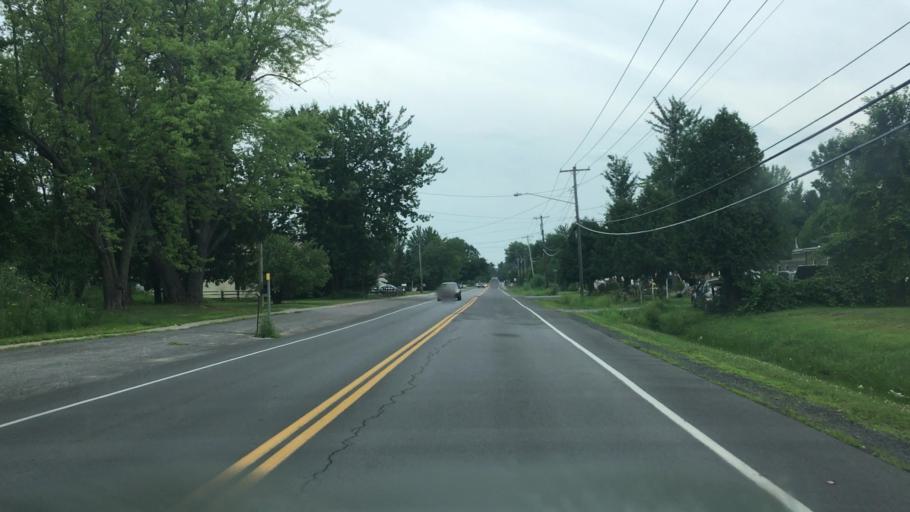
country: US
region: New York
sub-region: Clinton County
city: Plattsburgh West
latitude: 44.6839
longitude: -73.5069
